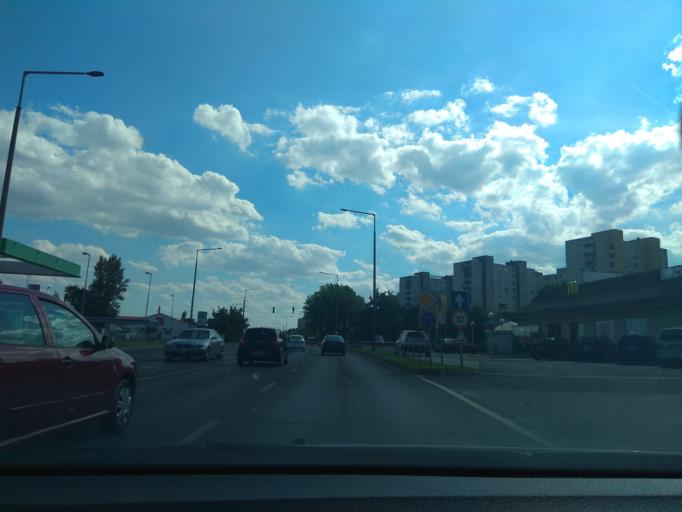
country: HU
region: Borsod-Abauj-Zemplen
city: Miskolc
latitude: 48.0835
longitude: 20.7861
